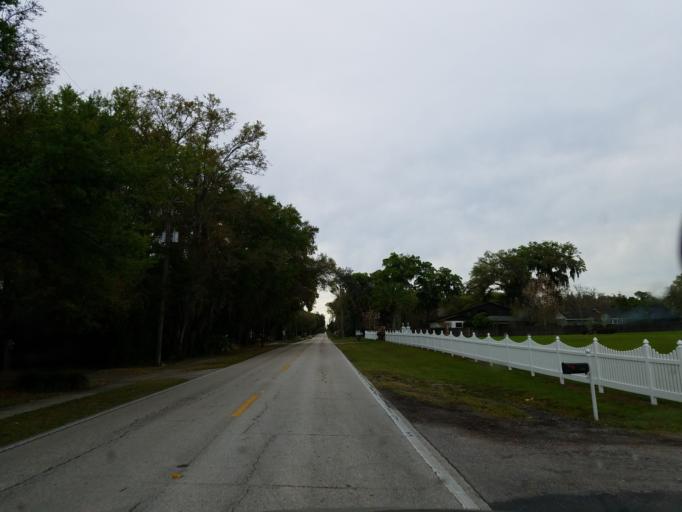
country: US
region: Florida
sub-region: Hillsborough County
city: Bloomingdale
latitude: 27.9159
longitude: -82.2444
